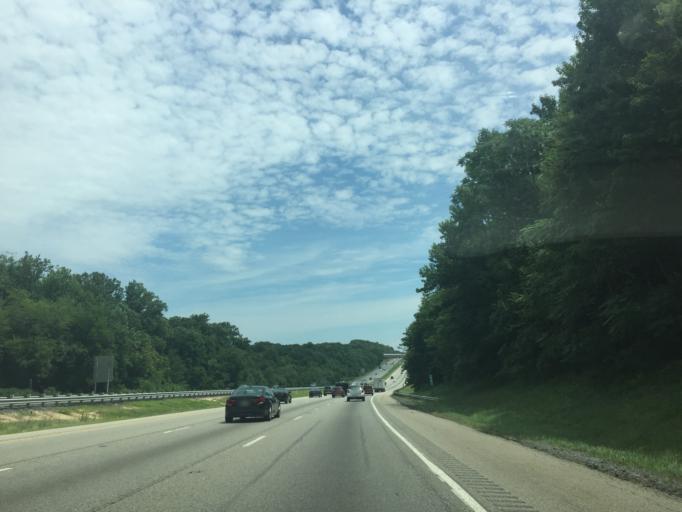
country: US
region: Maryland
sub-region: Cecil County
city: Perryville
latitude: 39.6049
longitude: -76.0346
